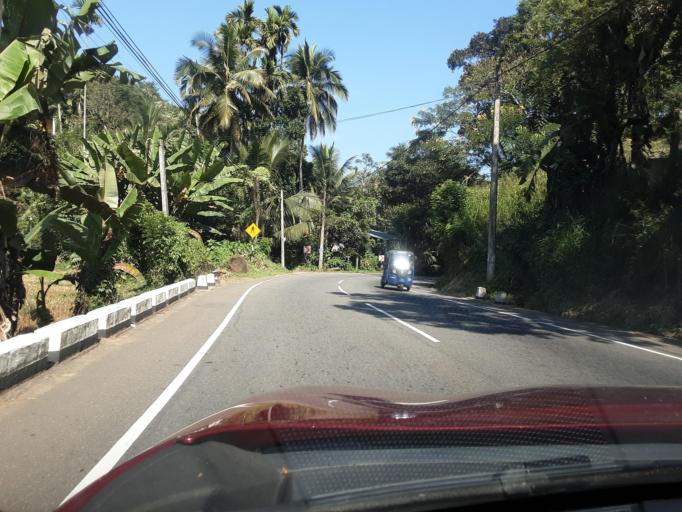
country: LK
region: Uva
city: Badulla
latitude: 7.0152
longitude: 81.0553
